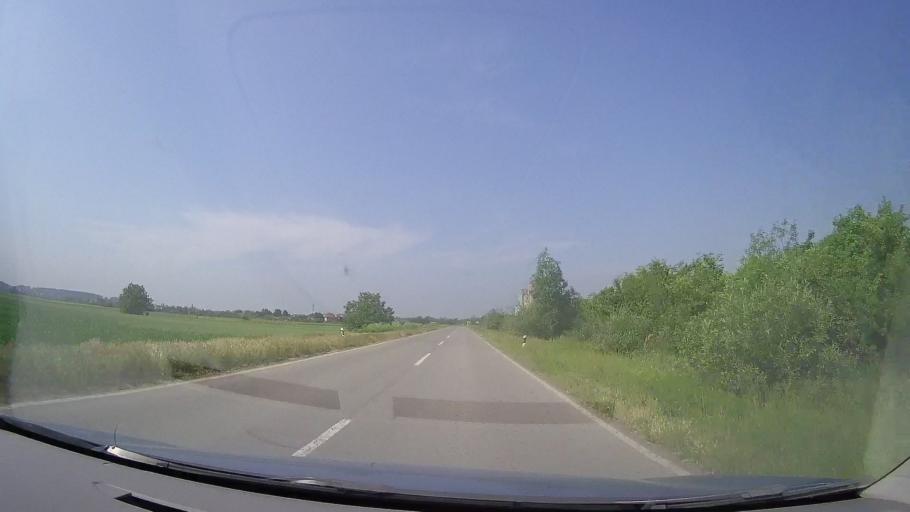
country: RS
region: Autonomna Pokrajina Vojvodina
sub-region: Srednjebanatski Okrug
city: Secanj
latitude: 45.3772
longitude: 20.7820
